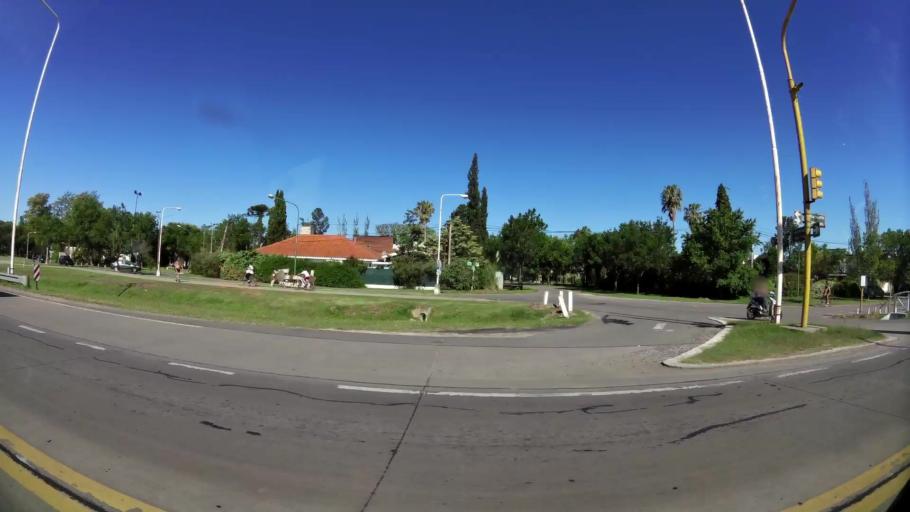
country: AR
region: Santa Fe
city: Rafaela
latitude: -31.2735
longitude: -61.5107
